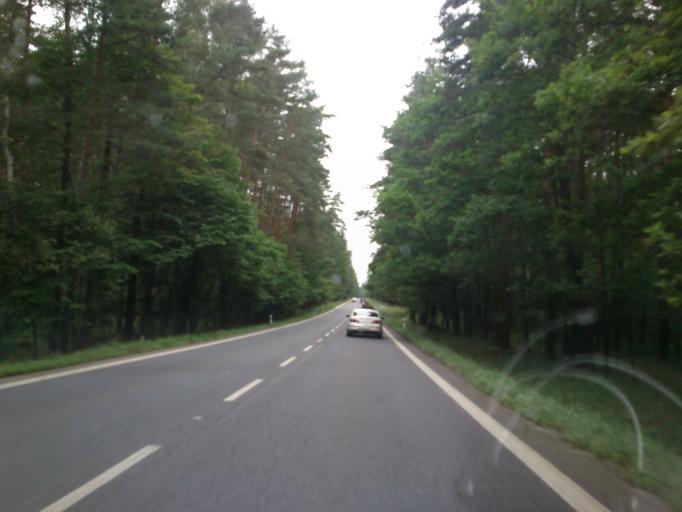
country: CZ
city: Doksy
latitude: 50.5342
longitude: 14.6868
